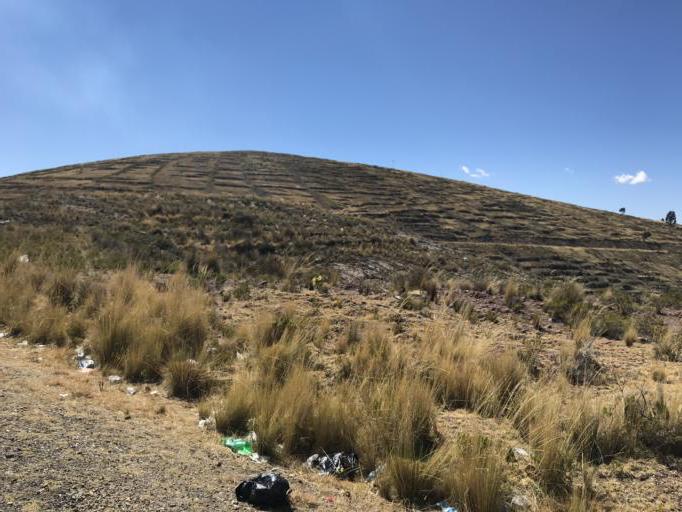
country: BO
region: La Paz
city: San Pablo
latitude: -16.2124
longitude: -68.8404
